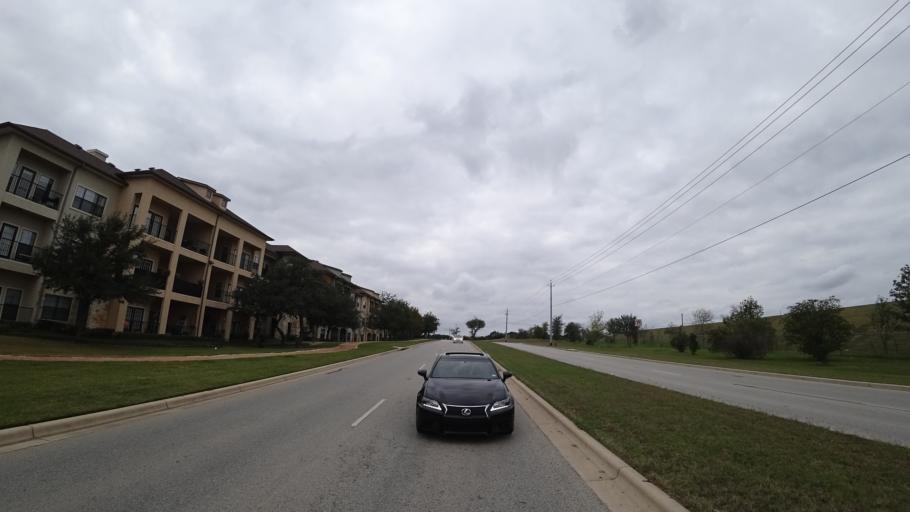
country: US
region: Texas
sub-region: Travis County
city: Bee Cave
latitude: 30.3110
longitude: -97.9398
